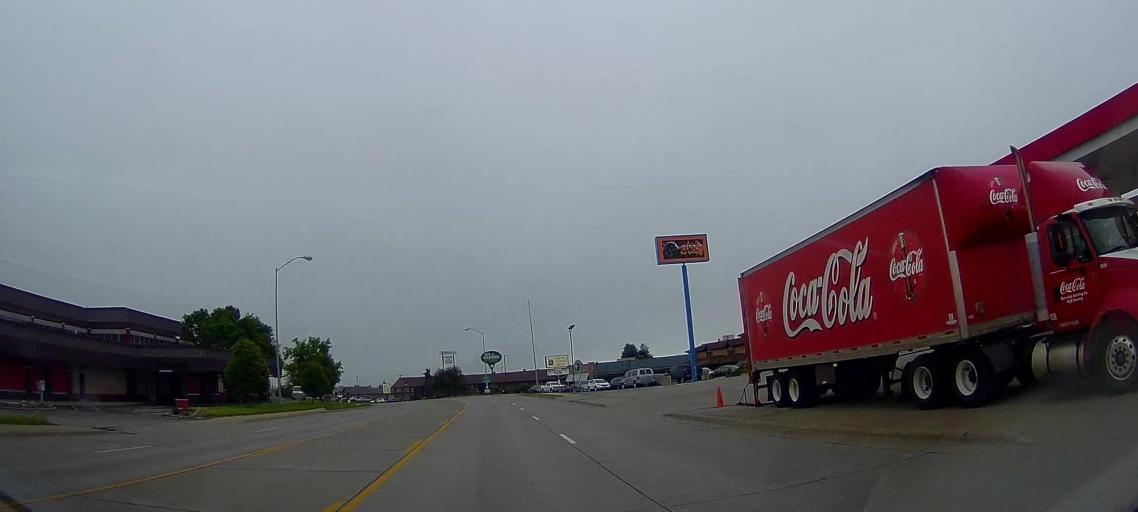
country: US
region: South Dakota
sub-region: Pennington County
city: Rapid City
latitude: 44.1030
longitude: -103.2036
